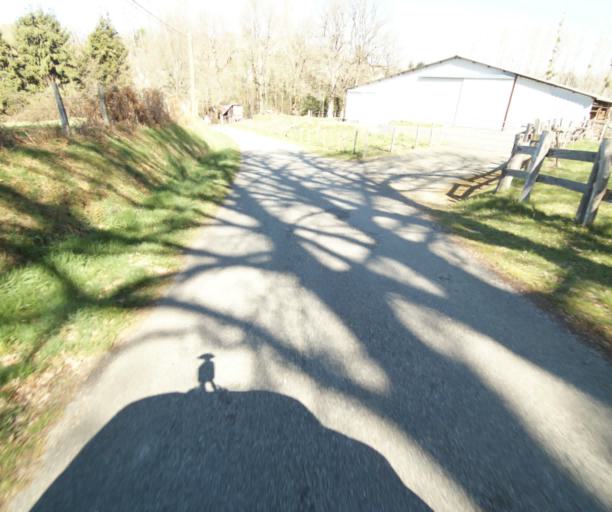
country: FR
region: Limousin
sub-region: Departement de la Correze
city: Seilhac
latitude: 45.3611
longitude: 1.7197
